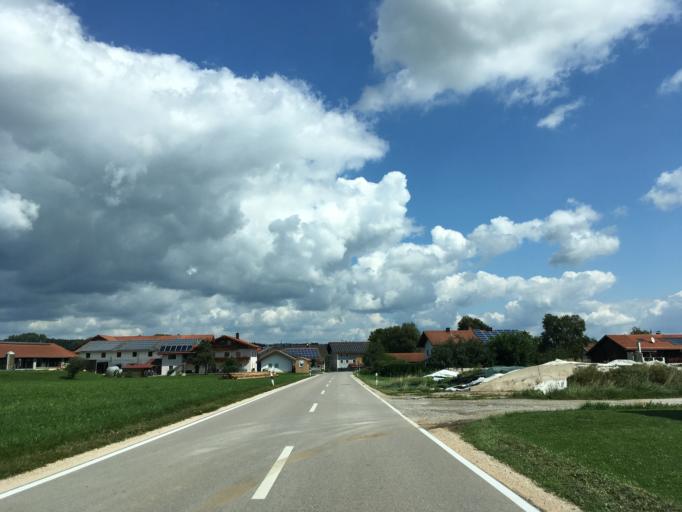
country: DE
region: Bavaria
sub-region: Upper Bavaria
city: Pittenhart
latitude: 47.9838
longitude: 12.3580
